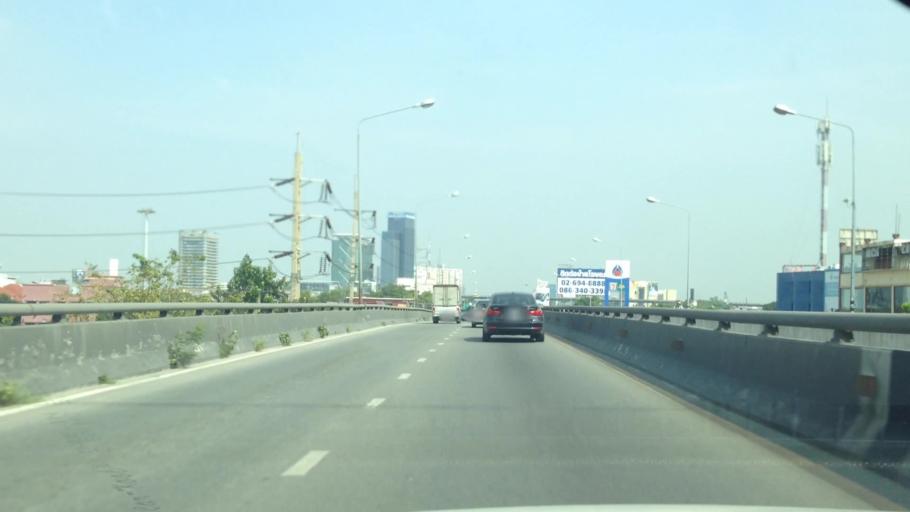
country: TH
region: Bangkok
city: Bang Na
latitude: 13.6560
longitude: 100.6423
